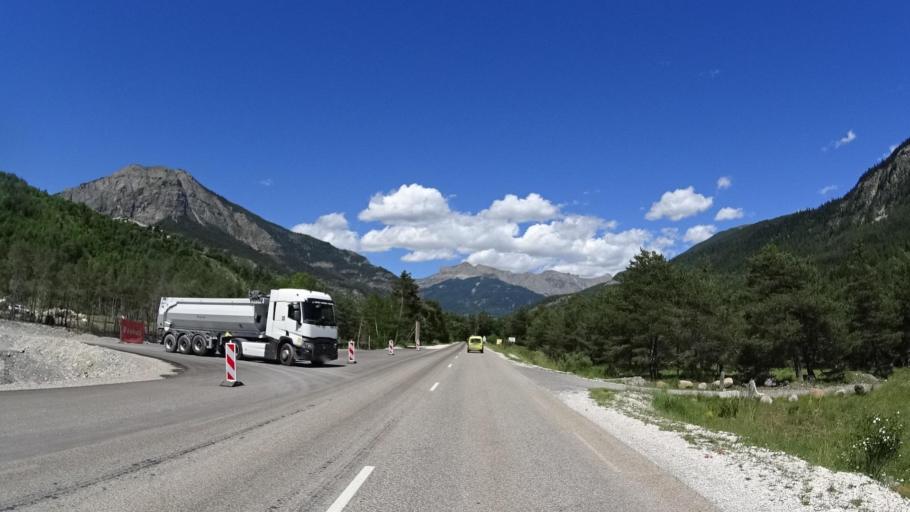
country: FR
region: Provence-Alpes-Cote d'Azur
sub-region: Departement des Alpes-de-Haute-Provence
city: Annot
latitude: 44.1570
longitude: 6.6013
